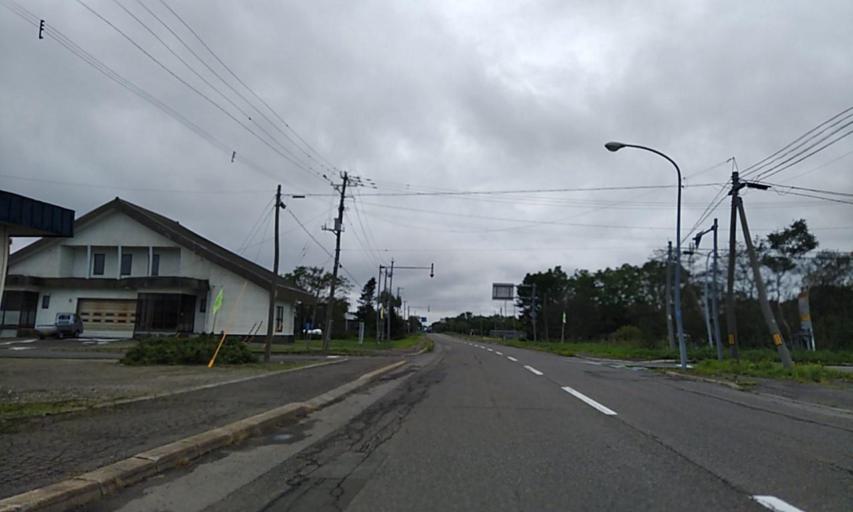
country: JP
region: Hokkaido
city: Nemuro
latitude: 43.3842
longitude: 145.2864
